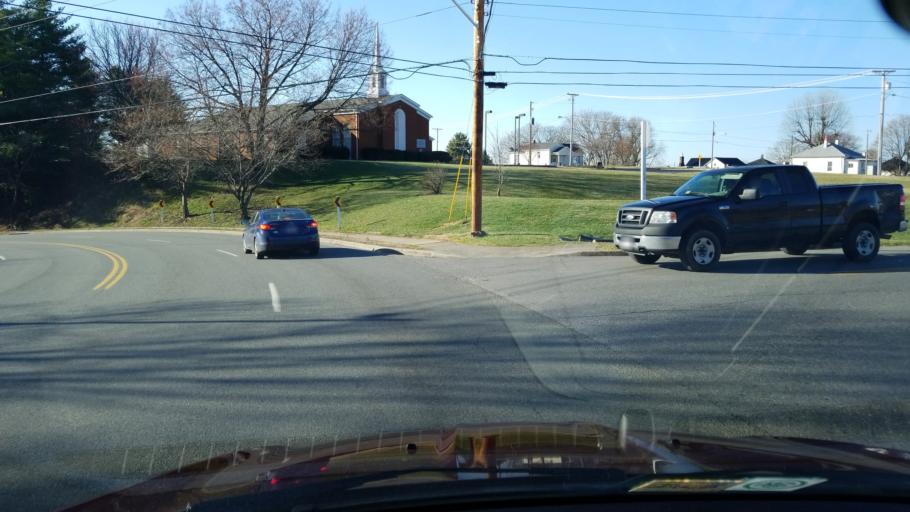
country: US
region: Virginia
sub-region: Franklin County
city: Rocky Mount
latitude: 37.0045
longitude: -79.8958
